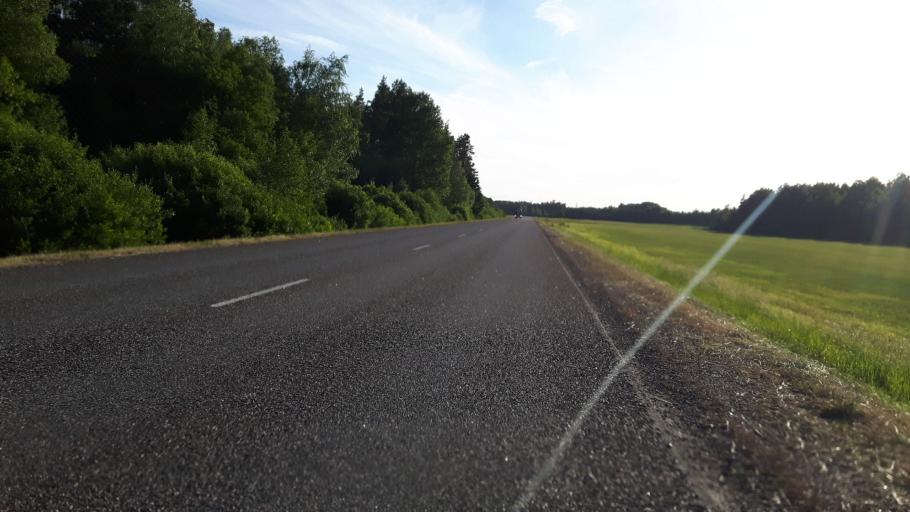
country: LV
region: Kuldigas Rajons
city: Kuldiga
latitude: 56.9943
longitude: 22.1046
